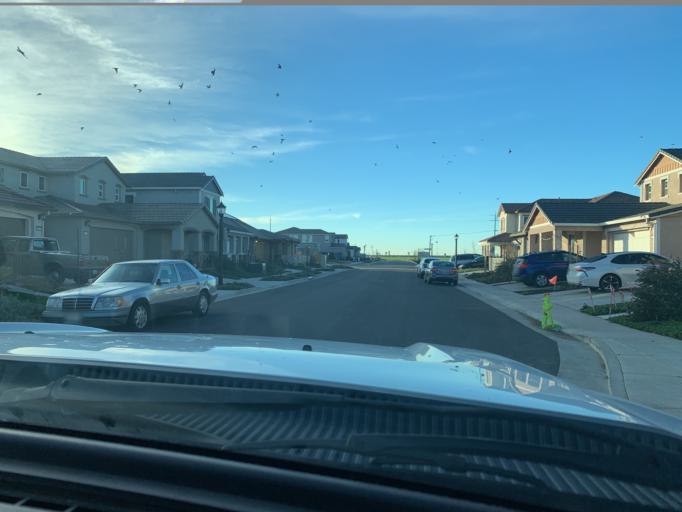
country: US
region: California
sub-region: Yolo County
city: Woodland
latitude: 38.6576
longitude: -121.7480
